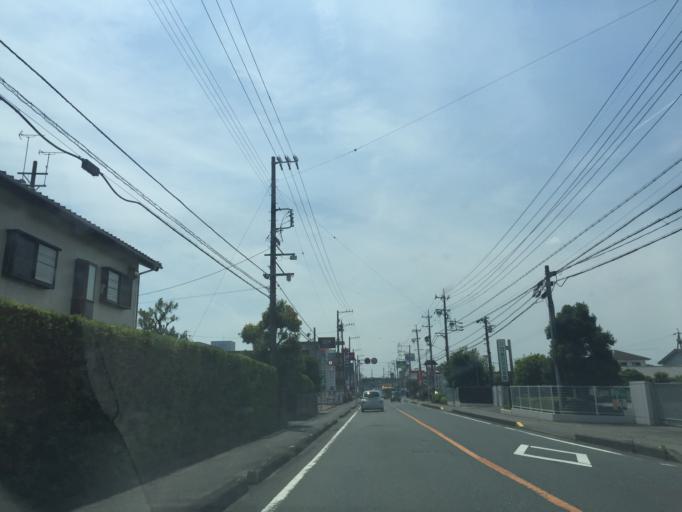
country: JP
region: Shizuoka
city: Kakegawa
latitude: 34.7790
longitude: 137.9832
